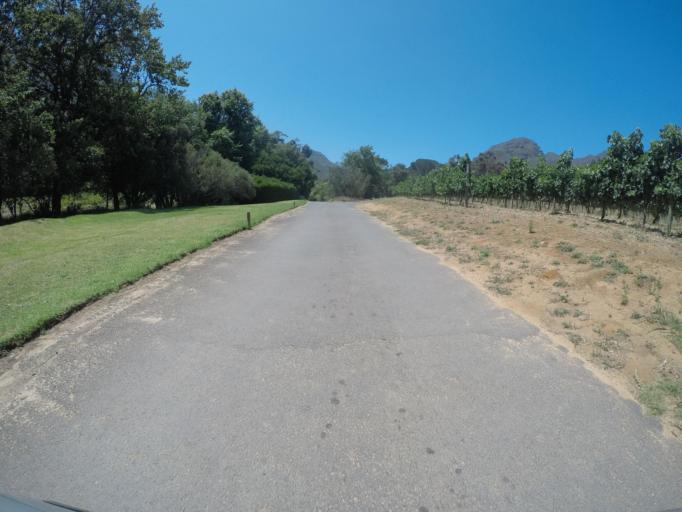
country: ZA
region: Western Cape
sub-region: Cape Winelands District Municipality
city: Stellenbosch
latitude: -34.0033
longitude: 18.8875
